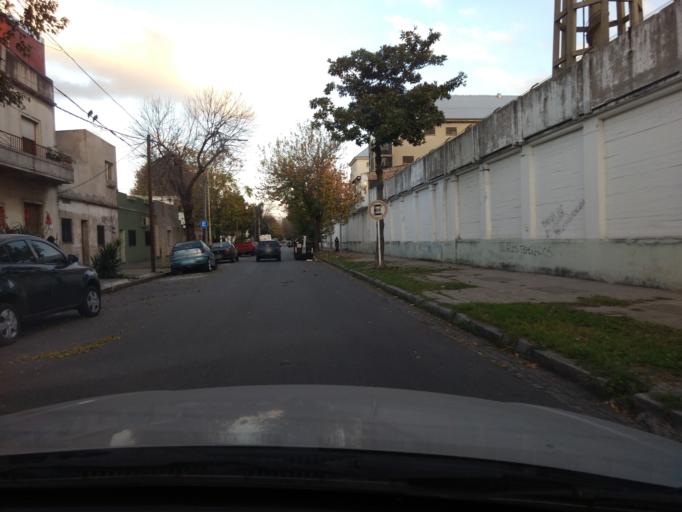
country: AR
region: Buenos Aires F.D.
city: Villa Santa Rita
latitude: -34.6137
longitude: -58.5138
